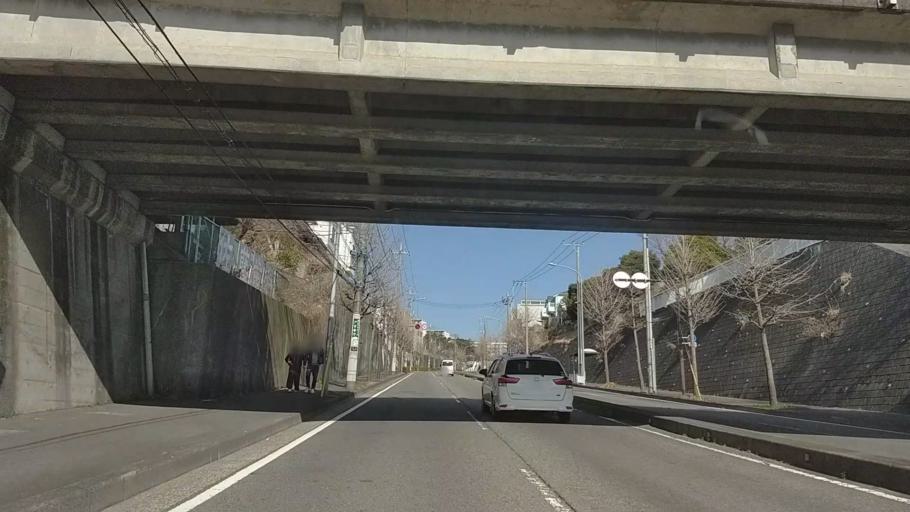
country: JP
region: Kanagawa
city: Kamakura
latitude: 35.3845
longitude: 139.5760
